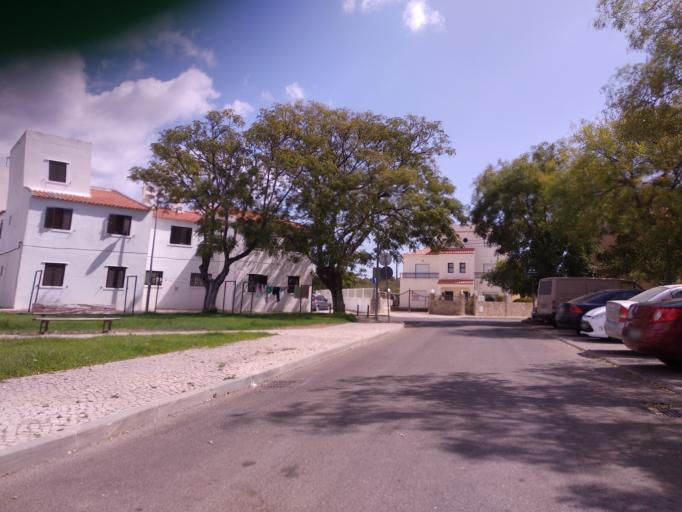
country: PT
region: Faro
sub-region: Sao Bras de Alportel
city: Sao Bras de Alportel
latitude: 37.1512
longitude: -7.8781
